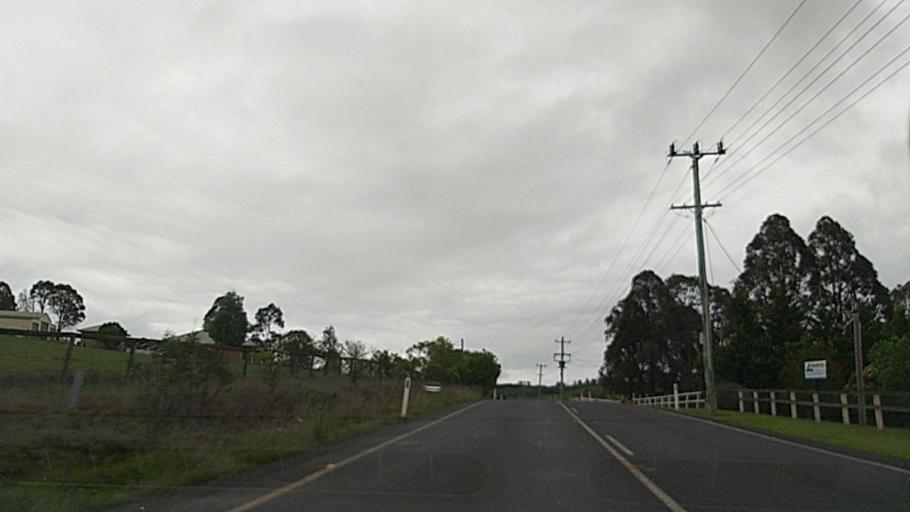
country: AU
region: New South Wales
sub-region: Wollondilly
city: Douglas Park
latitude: -34.1766
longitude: 150.7134
